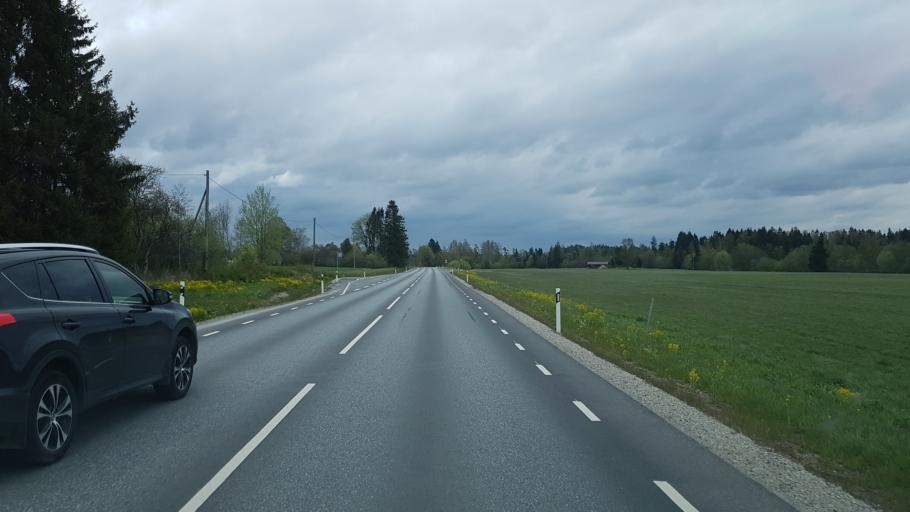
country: EE
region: Harju
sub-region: Anija vald
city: Kehra
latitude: 59.3730
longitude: 25.3147
